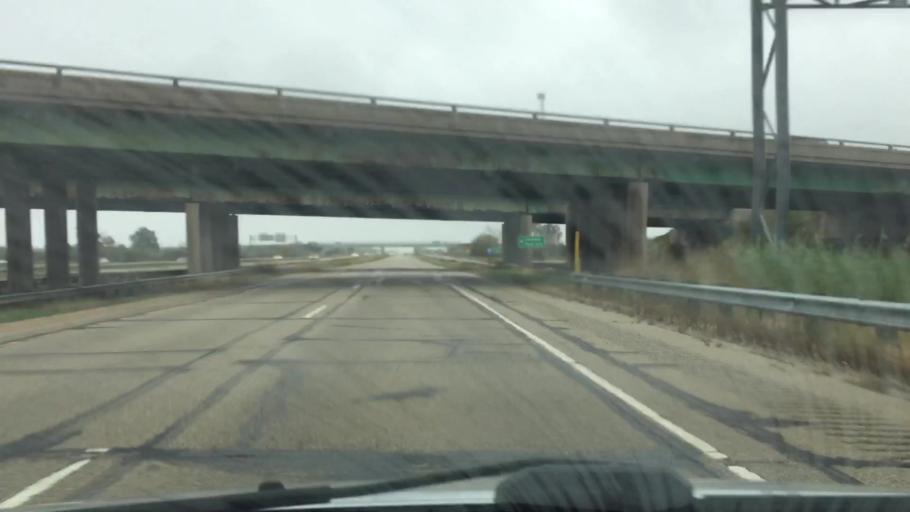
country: US
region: Wisconsin
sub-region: Walworth County
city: Elkhorn
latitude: 42.6747
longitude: -88.5222
